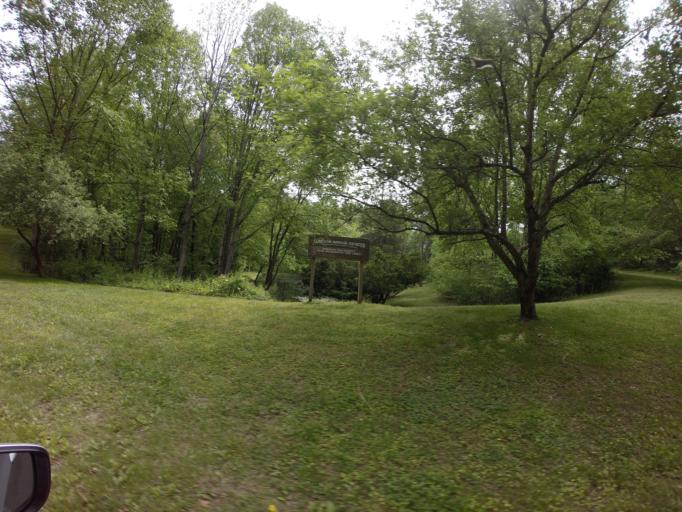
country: US
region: Maryland
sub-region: Carroll County
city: Eldersburg
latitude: 39.4619
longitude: -76.9579
